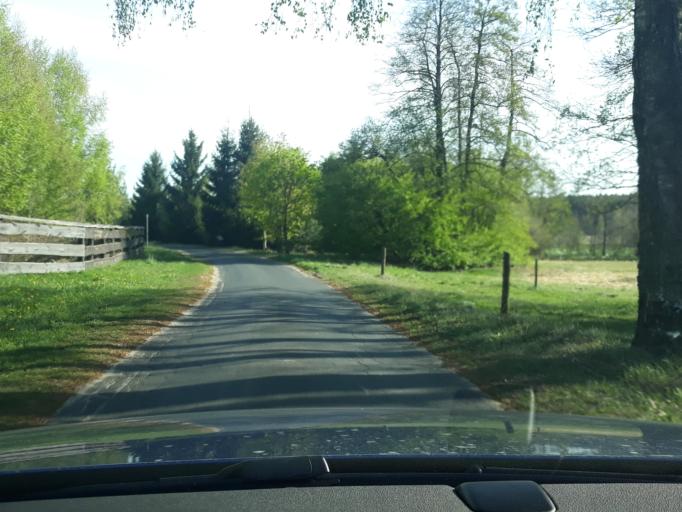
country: PL
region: Pomeranian Voivodeship
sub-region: Powiat czluchowski
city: Przechlewo
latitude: 53.8794
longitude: 17.3228
